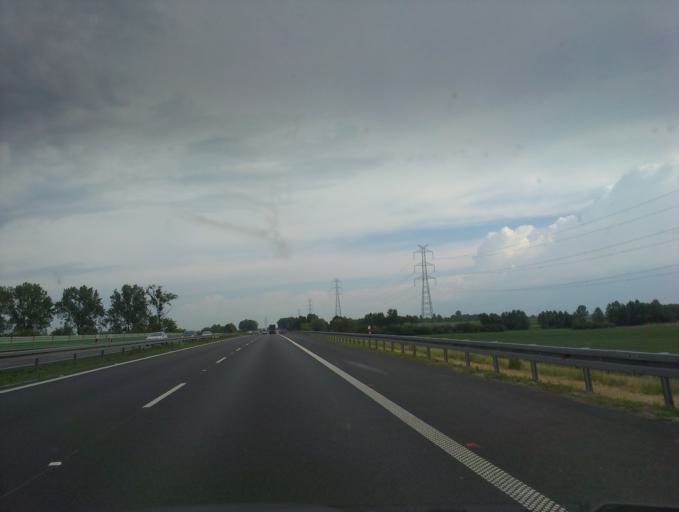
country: PL
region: Opole Voivodeship
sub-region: Powiat brzeski
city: Skarbimierz Osiedle
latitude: 50.8082
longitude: 17.3156
